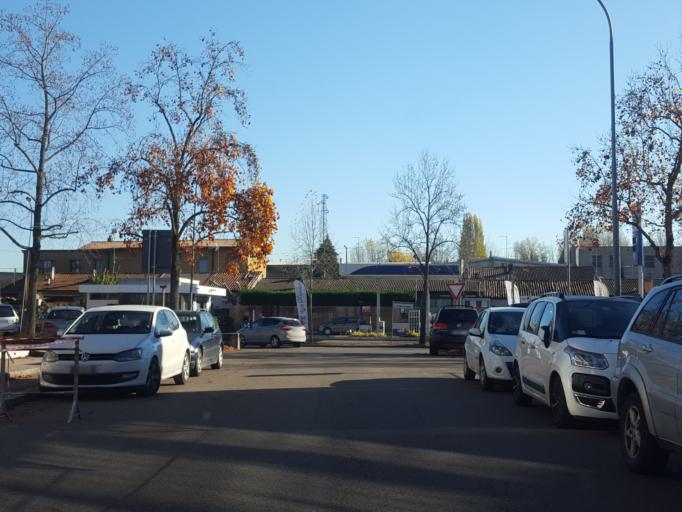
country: IT
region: Veneto
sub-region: Provincia di Verona
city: Verona
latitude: 45.4255
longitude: 10.9917
